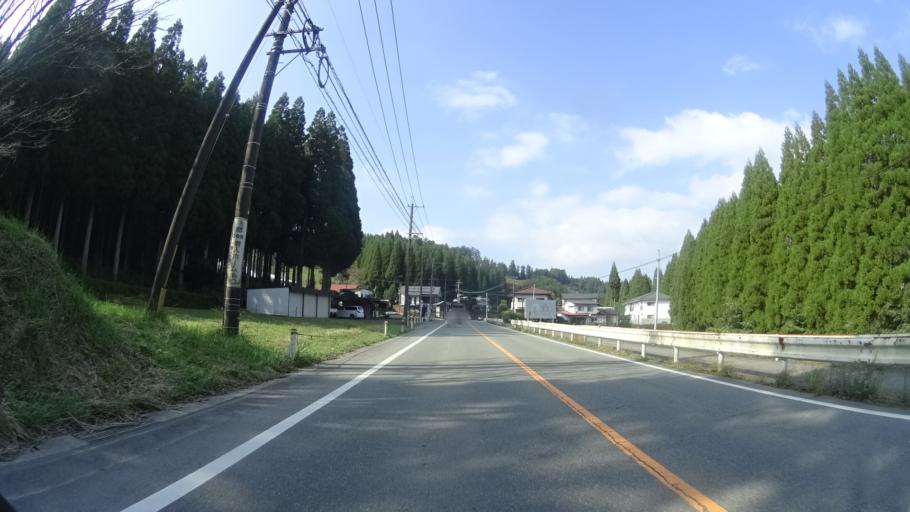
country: JP
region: Kumamoto
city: Aso
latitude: 33.1153
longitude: 131.0593
